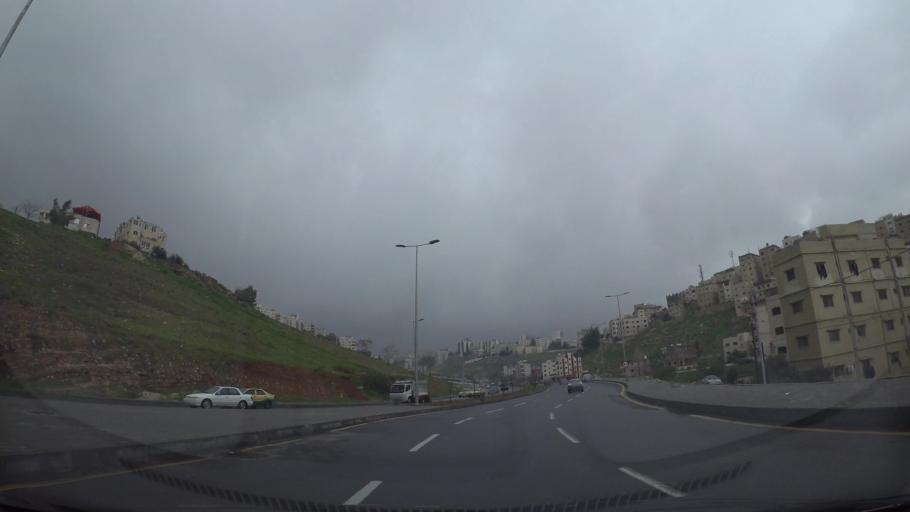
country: JO
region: Amman
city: Amman
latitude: 31.9401
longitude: 35.9076
